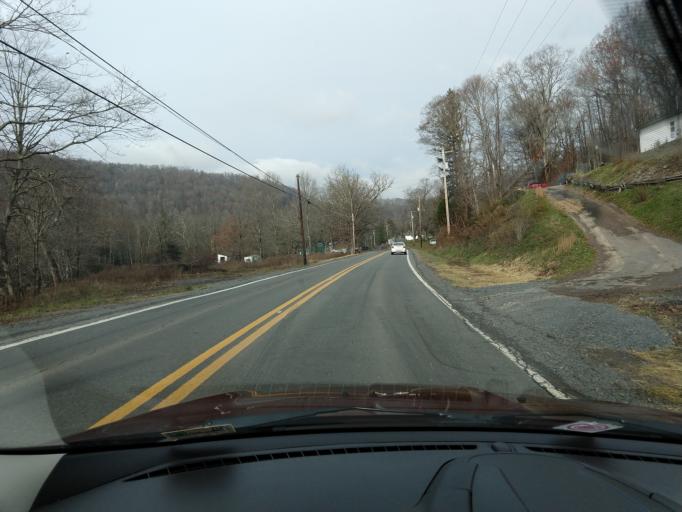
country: US
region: West Virginia
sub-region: Greenbrier County
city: Rainelle
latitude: 37.9881
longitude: -80.7288
